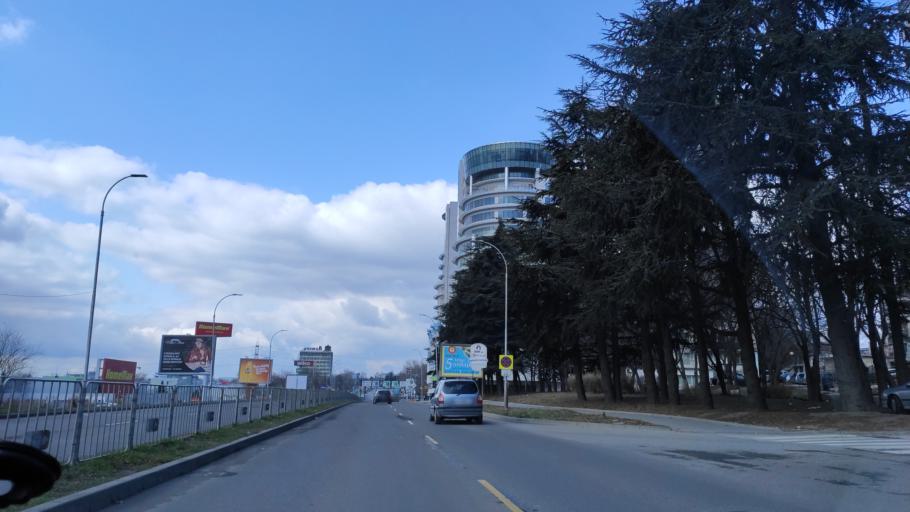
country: BG
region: Varna
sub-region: Obshtina Varna
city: Varna
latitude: 43.2212
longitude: 27.8789
